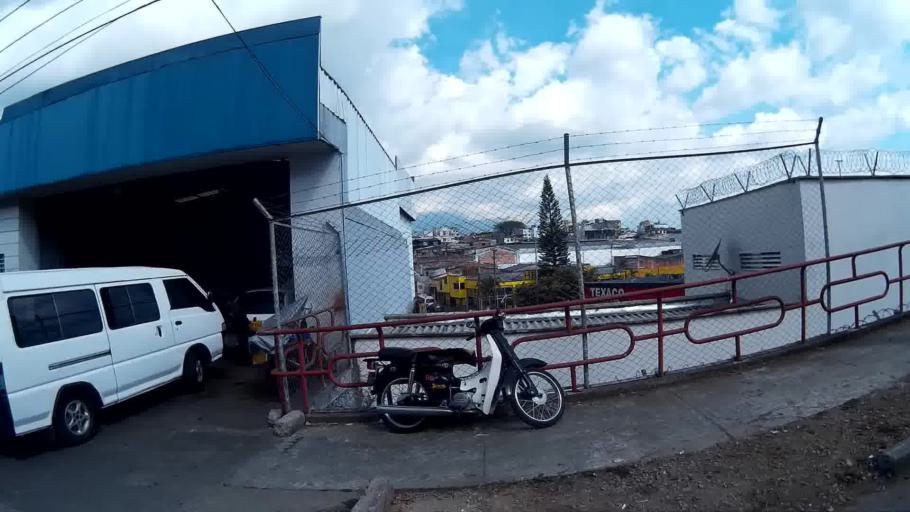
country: CO
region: Quindio
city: Armenia
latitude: 4.5405
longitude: -75.6703
